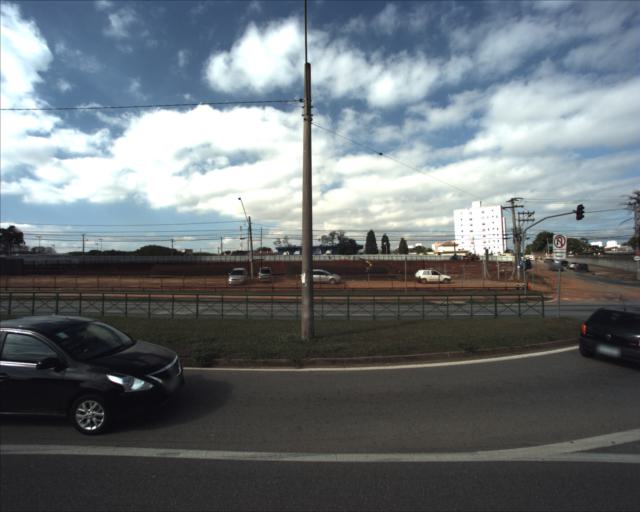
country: BR
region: Sao Paulo
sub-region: Sorocaba
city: Sorocaba
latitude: -23.5278
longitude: -47.4902
